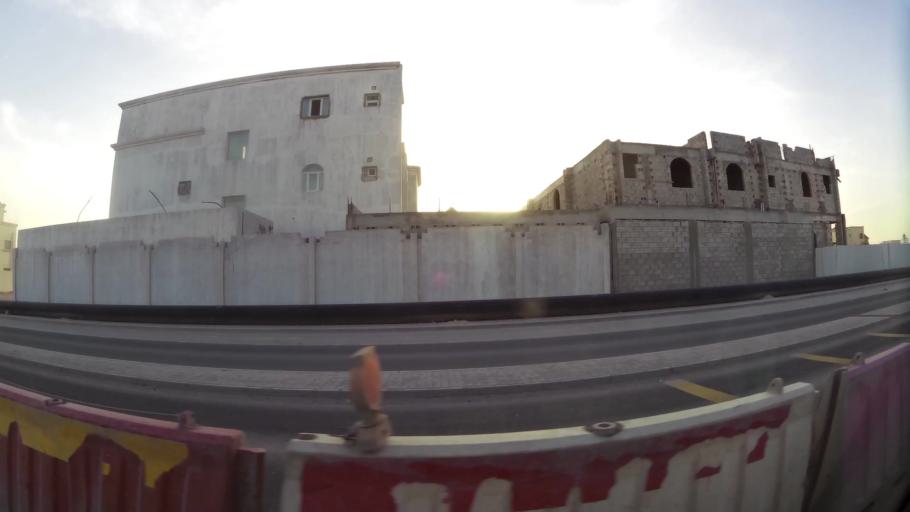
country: QA
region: Al Wakrah
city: Al Wakrah
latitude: 25.1571
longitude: 51.5922
